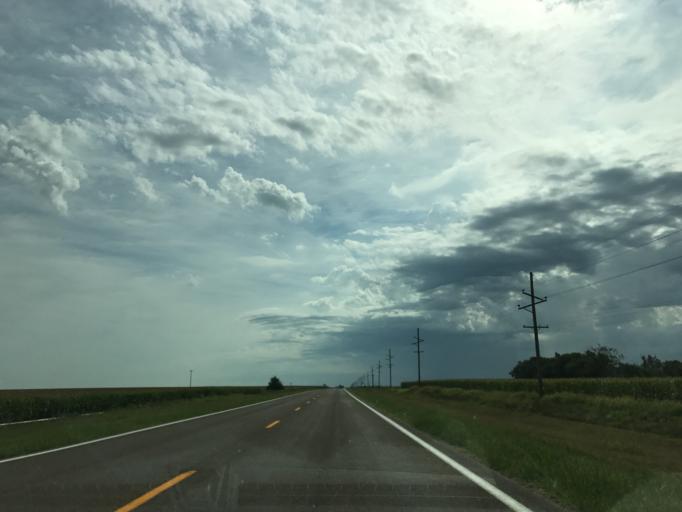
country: US
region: Nebraska
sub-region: Jefferson County
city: Fairbury
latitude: 40.3061
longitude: -97.1079
